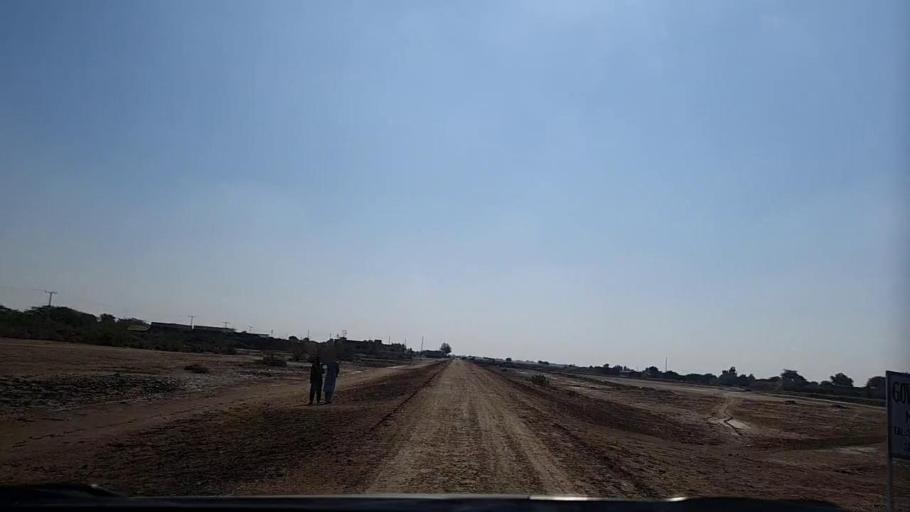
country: PK
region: Sindh
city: Pithoro
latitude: 25.6952
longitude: 69.3557
